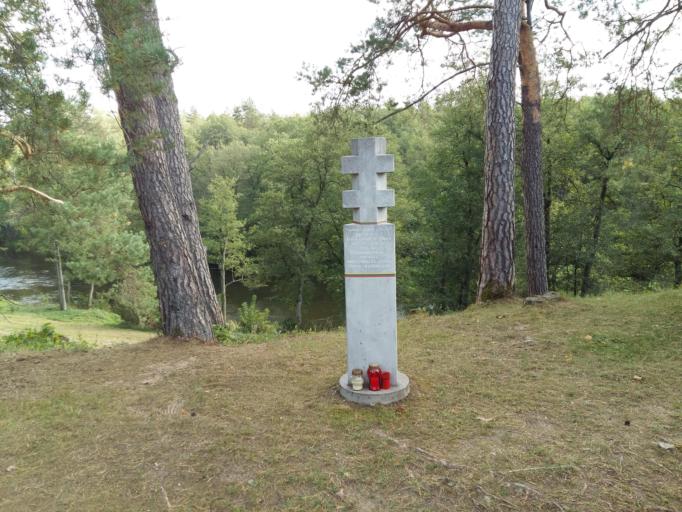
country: LT
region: Alytaus apskritis
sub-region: Alytaus rajonas
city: Daugai
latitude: 54.1168
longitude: 24.2796
